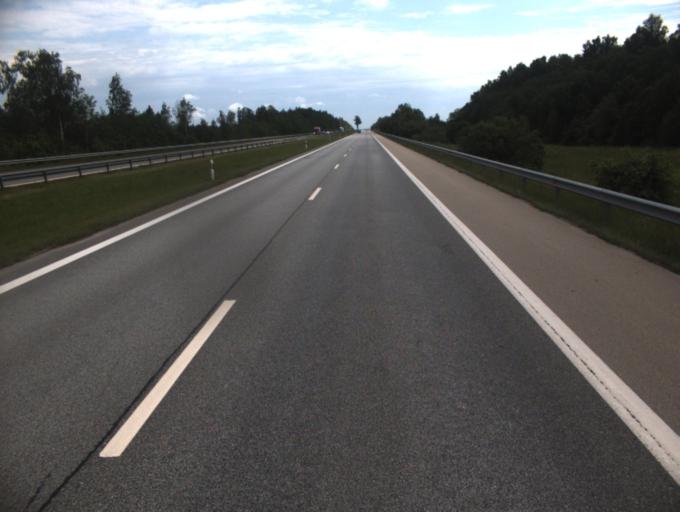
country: LT
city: Raseiniai
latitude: 55.3067
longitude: 23.2503
